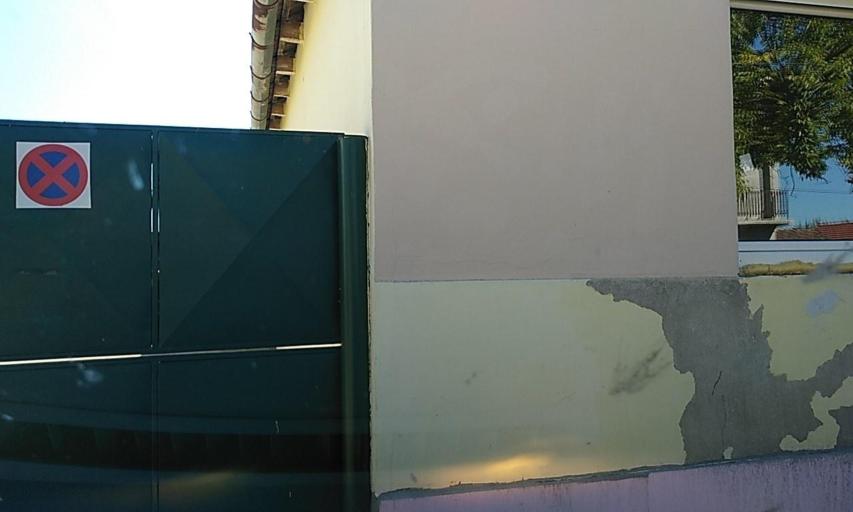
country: RS
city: Backo Gradiste
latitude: 45.5428
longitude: 20.0349
